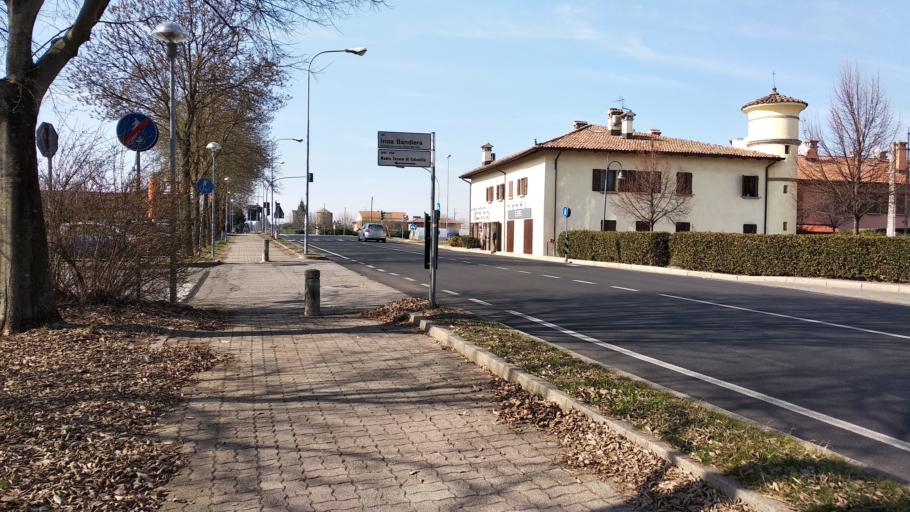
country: IT
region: Emilia-Romagna
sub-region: Provincia di Bologna
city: Ozzano dell'Emilia
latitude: 44.4485
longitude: 11.4666
